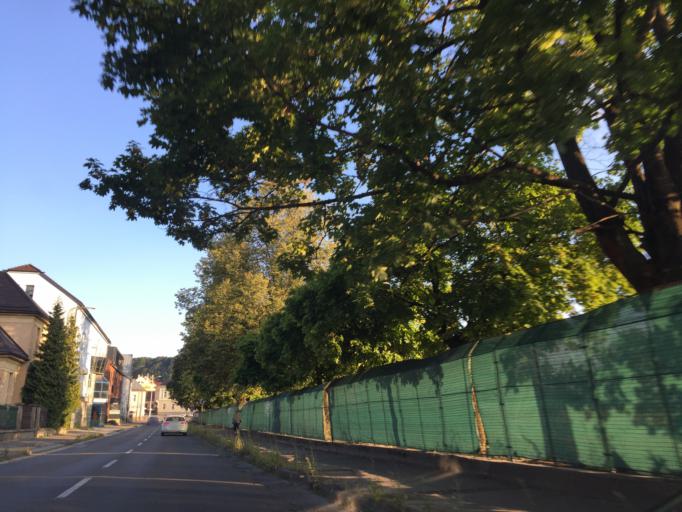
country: SK
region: Banskobystricky
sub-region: Okres Banska Bystrica
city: Banska Bystrica
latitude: 48.7389
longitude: 19.1413
